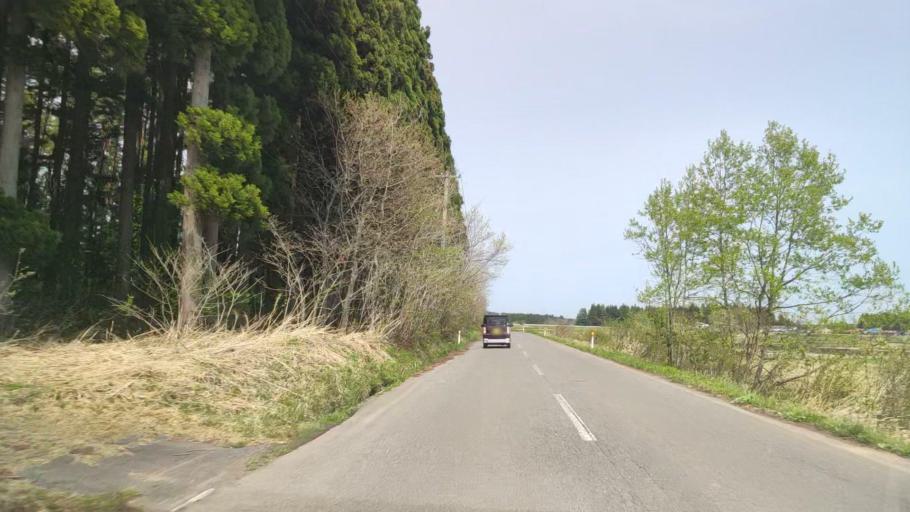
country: JP
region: Aomori
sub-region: Misawa Shi
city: Inuotose
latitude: 40.7687
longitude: 141.1218
